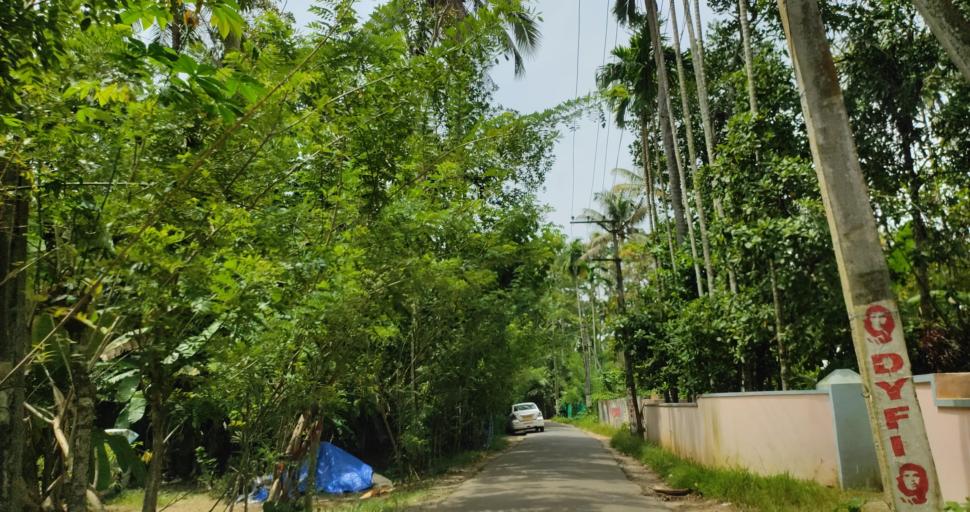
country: IN
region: Kerala
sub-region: Alappuzha
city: Shertallai
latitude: 9.6817
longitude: 76.3594
